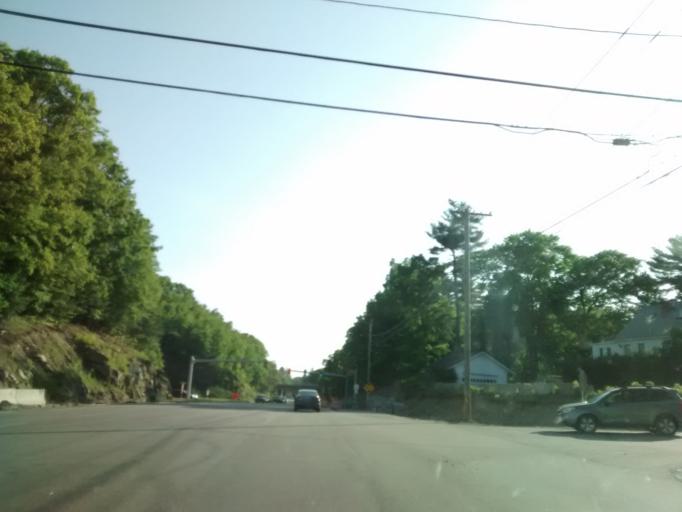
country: US
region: Massachusetts
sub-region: Worcester County
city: Berlin
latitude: 42.3964
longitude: -71.6038
